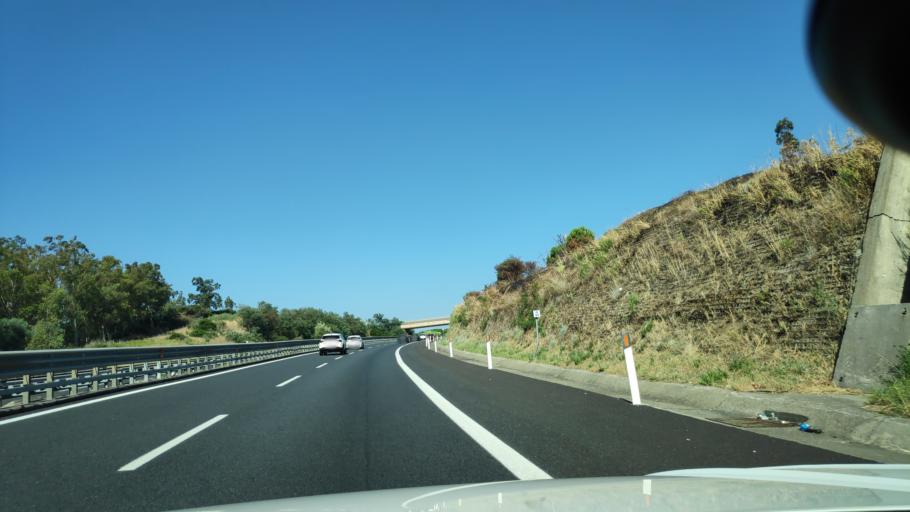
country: IT
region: Calabria
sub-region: Provincia di Catanzaro
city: Falerna Scalo
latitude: 38.9510
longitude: 16.1638
